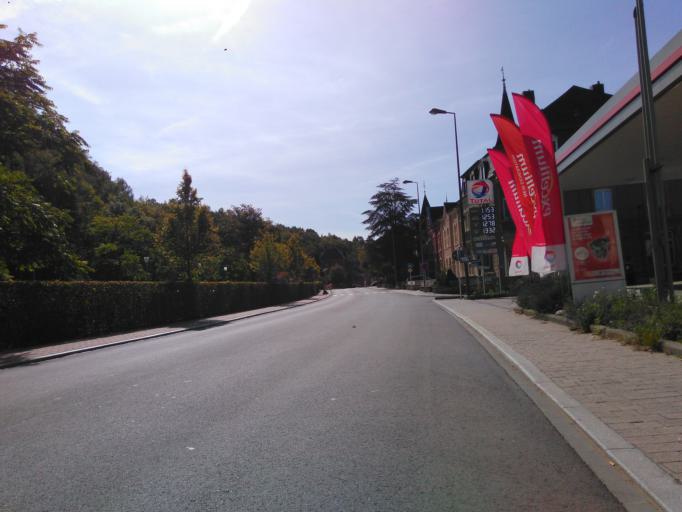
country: LU
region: Luxembourg
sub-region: Canton d'Esch-sur-Alzette
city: Rumelange
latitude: 49.4585
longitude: 6.0313
